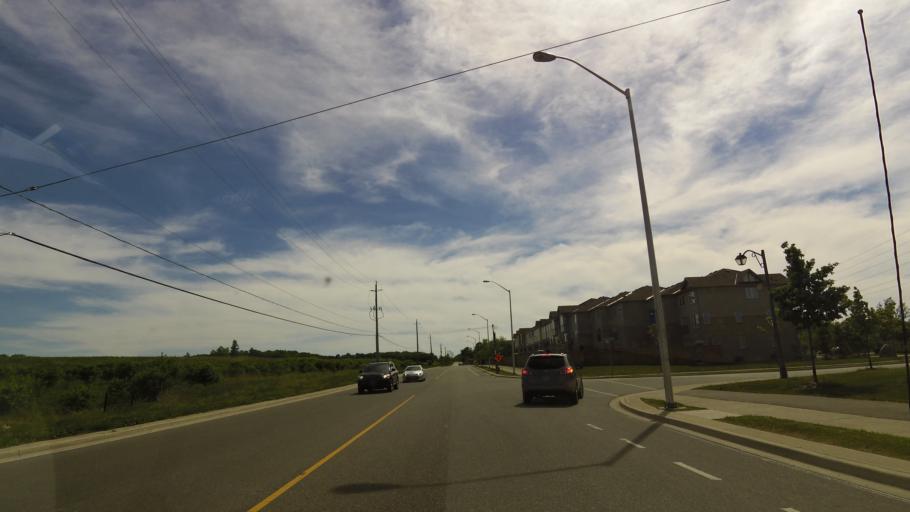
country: CA
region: Ontario
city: Oakville
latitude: 43.4218
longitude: -79.7602
